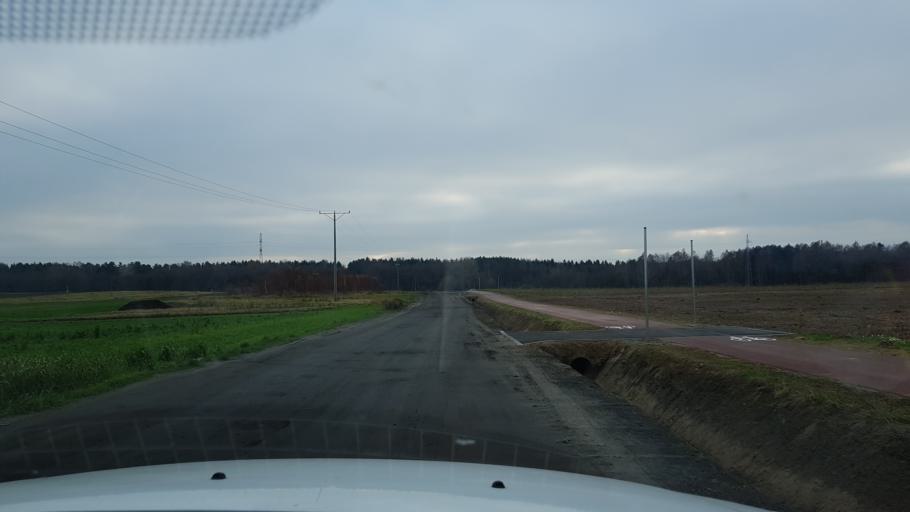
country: PL
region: West Pomeranian Voivodeship
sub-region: Powiat kolobrzeski
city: Grzybowo
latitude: 54.1393
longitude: 15.5147
